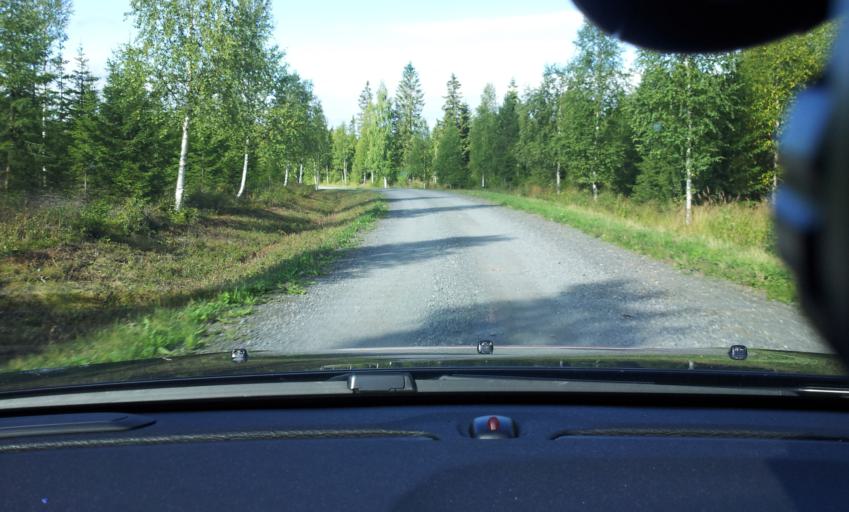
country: SE
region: Jaemtland
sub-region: Krokoms Kommun
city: Valla
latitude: 63.2633
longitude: 13.7943
